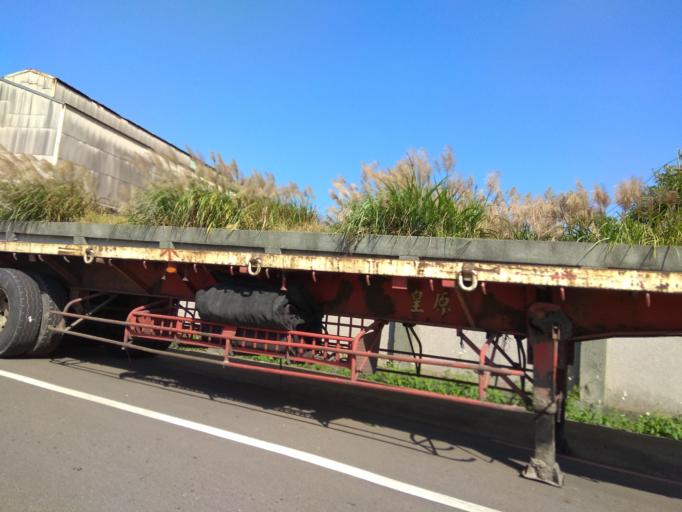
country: TW
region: Taiwan
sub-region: Hsinchu
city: Zhubei
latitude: 24.9798
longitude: 121.0390
